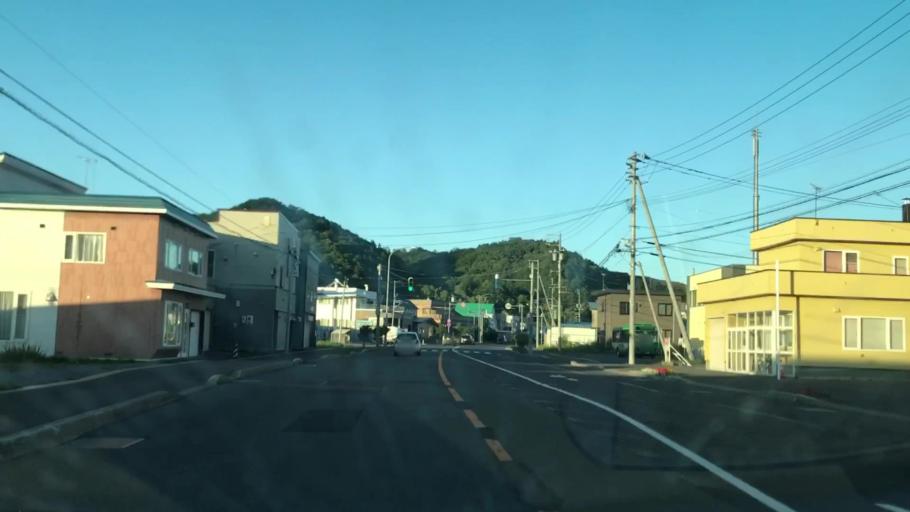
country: JP
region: Hokkaido
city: Niseko Town
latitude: 42.7953
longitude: 140.9382
